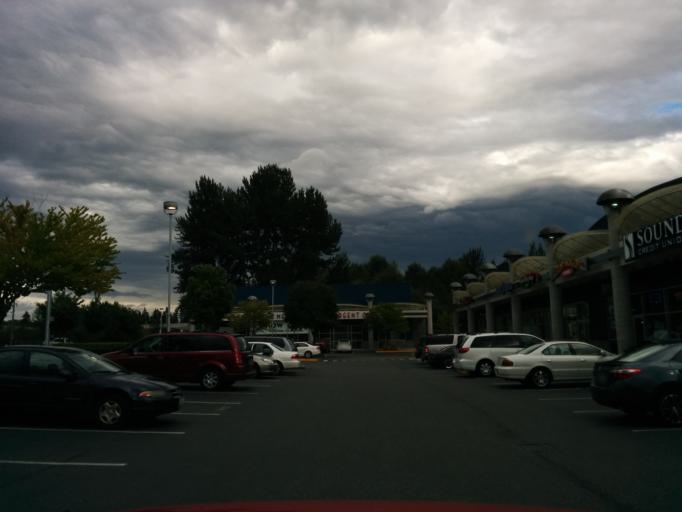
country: US
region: Washington
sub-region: King County
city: Redmond
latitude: 47.6705
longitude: -122.1113
